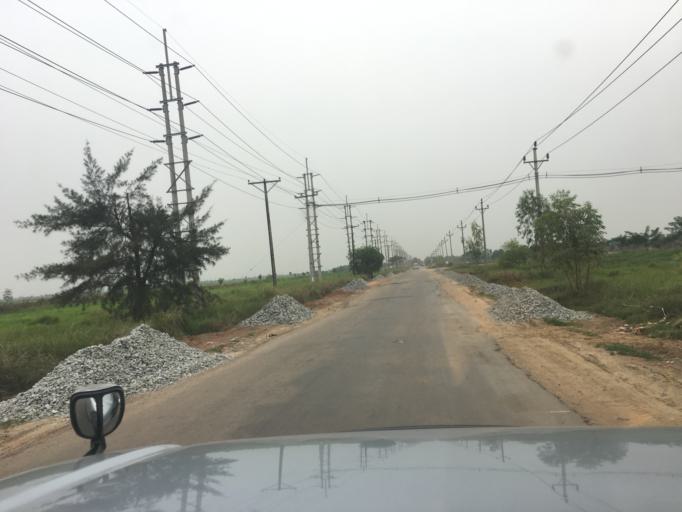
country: MM
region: Yangon
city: Syriam
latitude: 16.9545
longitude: 96.2697
